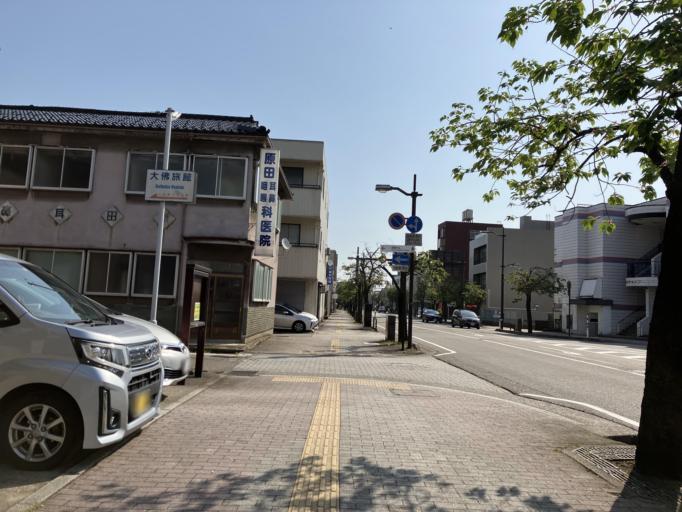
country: JP
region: Toyama
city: Takaoka
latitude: 36.7438
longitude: 137.0178
